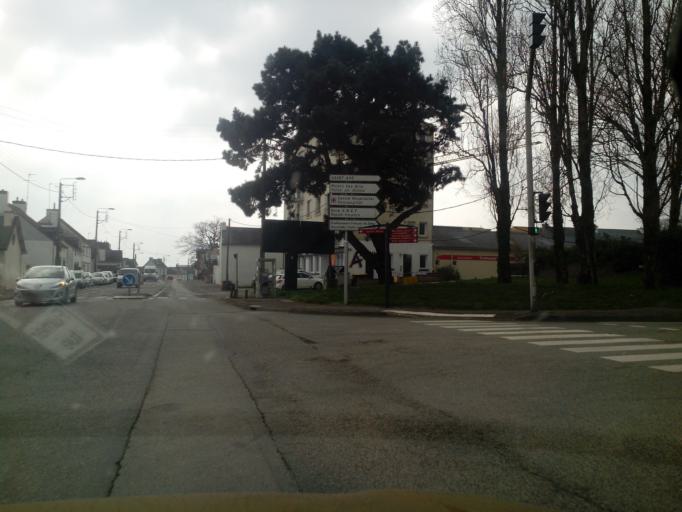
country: FR
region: Brittany
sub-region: Departement du Morbihan
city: Vannes
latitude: 47.6648
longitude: -2.7374
